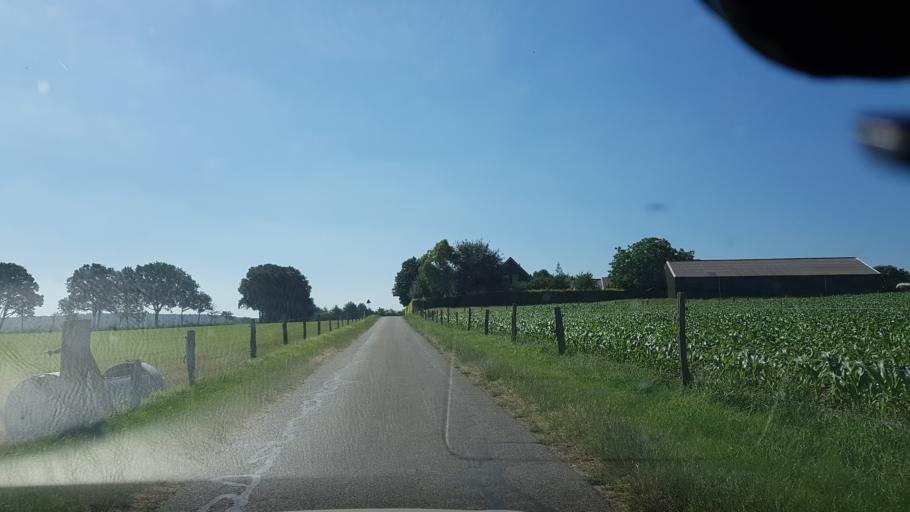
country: NL
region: Gelderland
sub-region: Gemeente Groesbeek
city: Bredeweg
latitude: 51.7528
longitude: 5.9304
